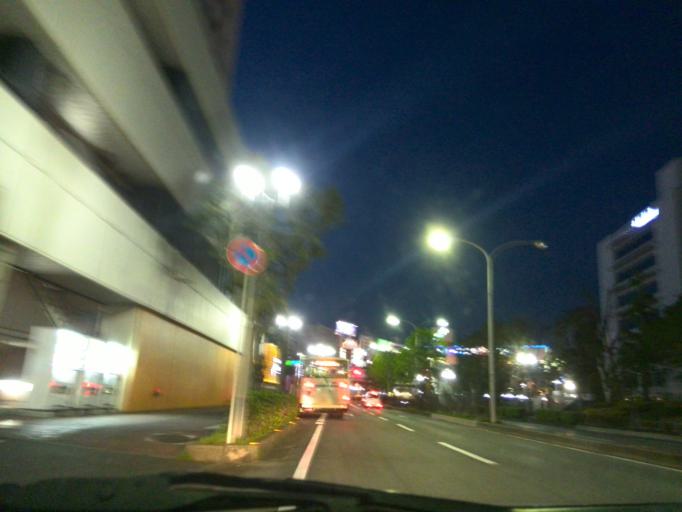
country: JP
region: Chiba
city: Funabashi
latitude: 35.6893
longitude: 140.0199
